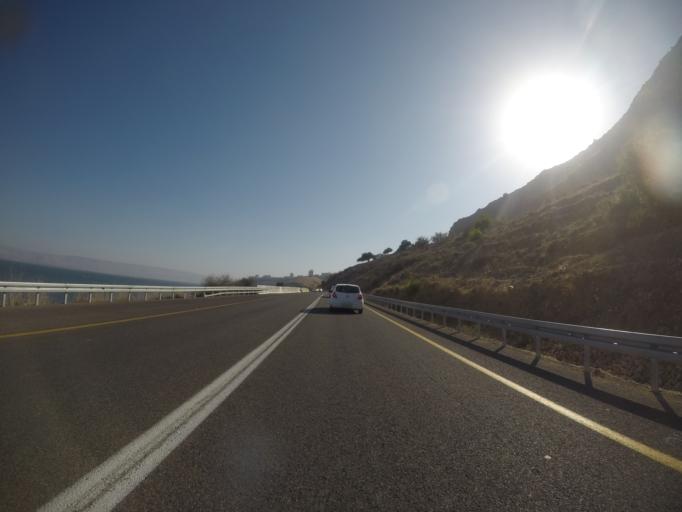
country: IL
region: Northern District
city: Tiberias
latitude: 32.8165
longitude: 35.5203
